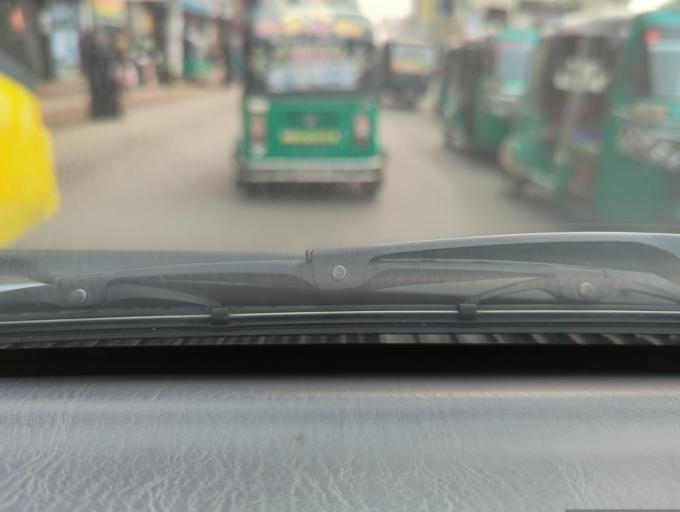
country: BD
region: Sylhet
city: Maulavi Bazar
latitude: 24.4853
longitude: 91.7656
